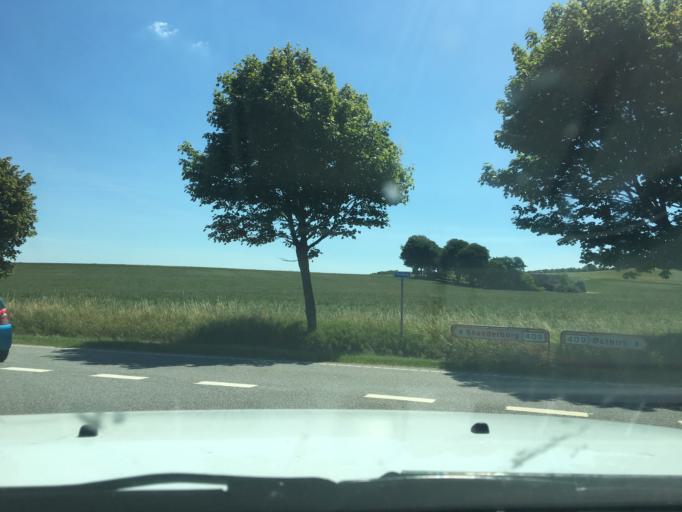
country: DK
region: Central Jutland
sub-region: Skanderborg Kommune
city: Ry
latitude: 56.0223
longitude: 9.8215
